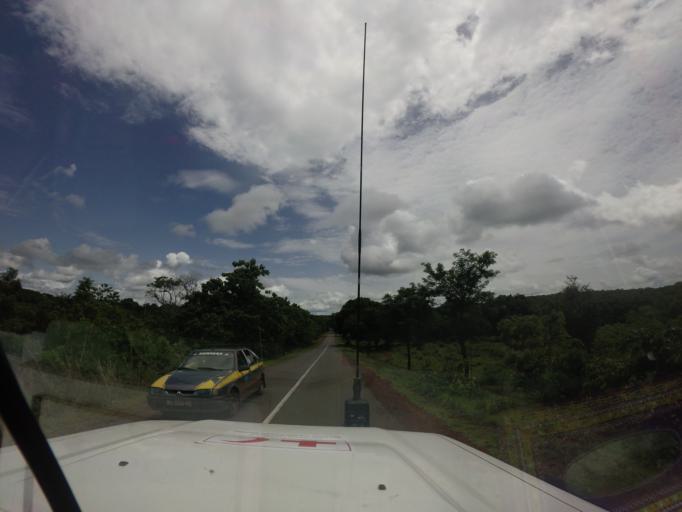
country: GN
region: Faranah
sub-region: Faranah Prefecture
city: Faranah
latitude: 10.0184
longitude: -10.9589
